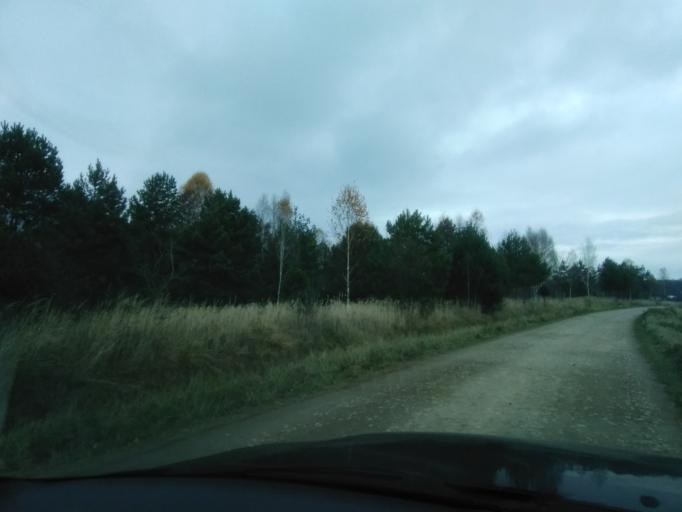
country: PL
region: Subcarpathian Voivodeship
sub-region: Powiat strzyzowski
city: Wysoka Strzyzowska
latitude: 49.8033
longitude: 21.7814
